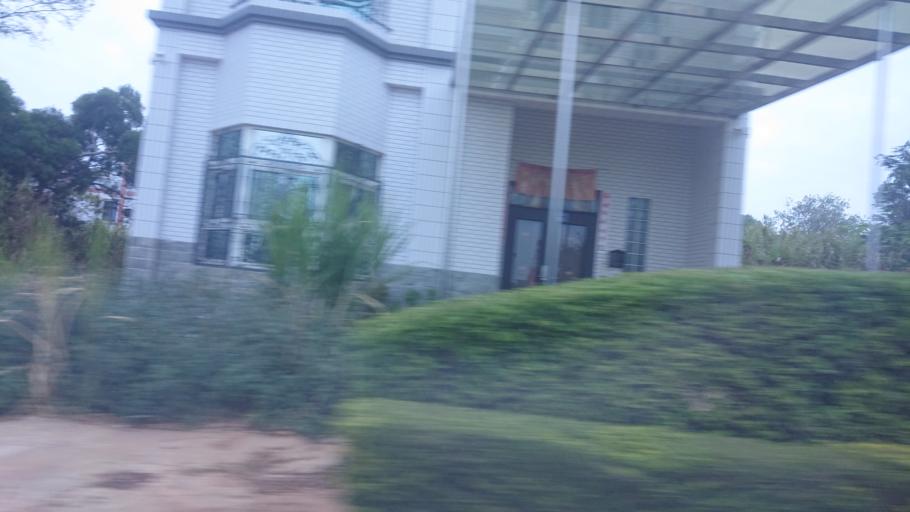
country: TW
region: Fukien
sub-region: Kinmen
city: Jincheng
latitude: 24.4113
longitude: 118.2988
